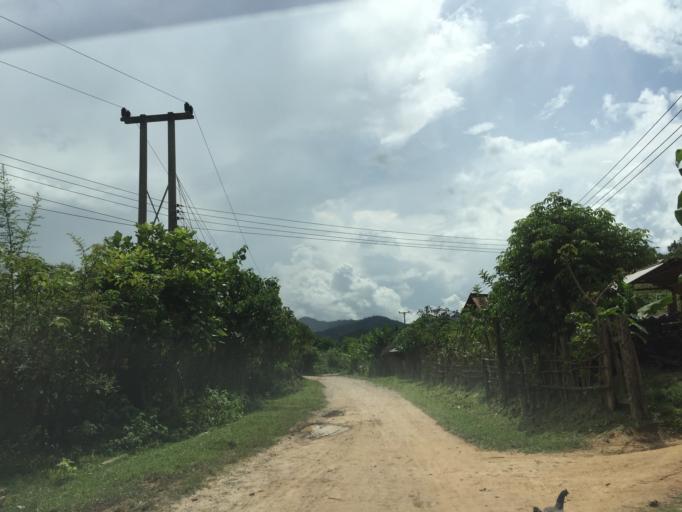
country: LA
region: Xiangkhoang
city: Muang Phonsavan
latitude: 19.3411
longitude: 103.5443
